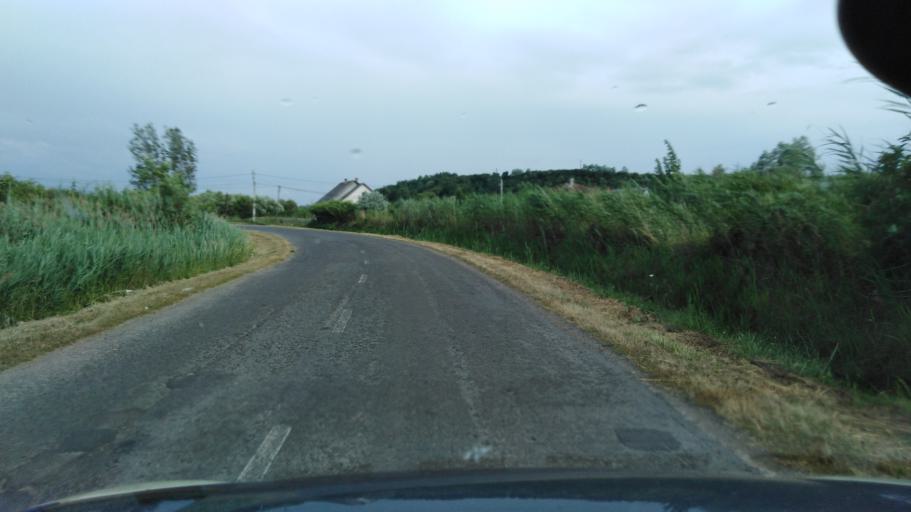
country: HU
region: Nograd
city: Karancskeszi
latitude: 48.2075
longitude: 19.5909
